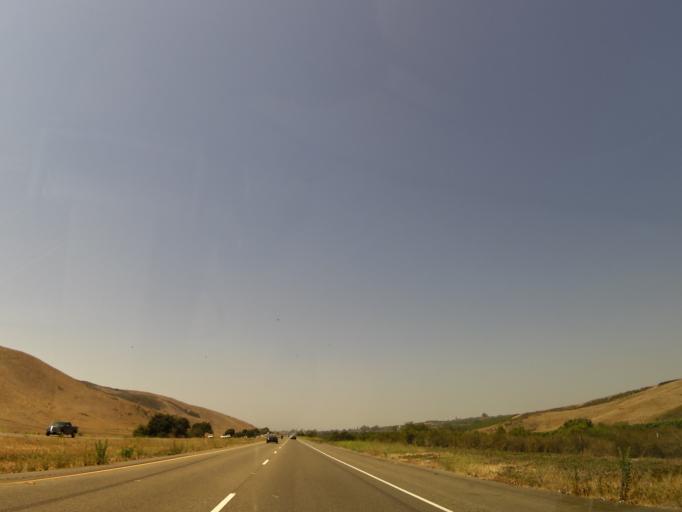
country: US
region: California
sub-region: Santa Barbara County
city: Orcutt
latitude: 34.8329
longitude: -120.3672
